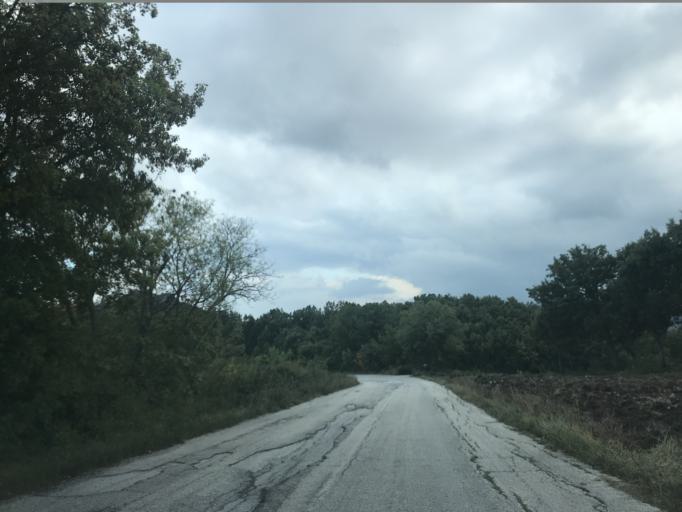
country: IT
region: Molise
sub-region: Provincia di Campobasso
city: Duronia
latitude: 41.6761
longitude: 14.4531
